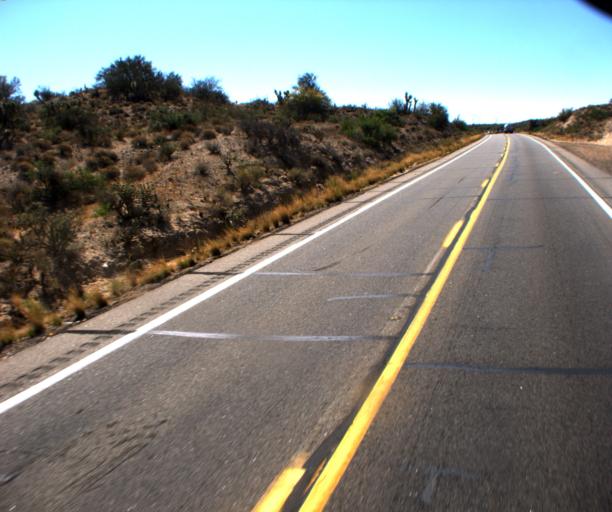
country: US
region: Arizona
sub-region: Yavapai County
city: Bagdad
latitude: 34.3491
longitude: -113.1630
